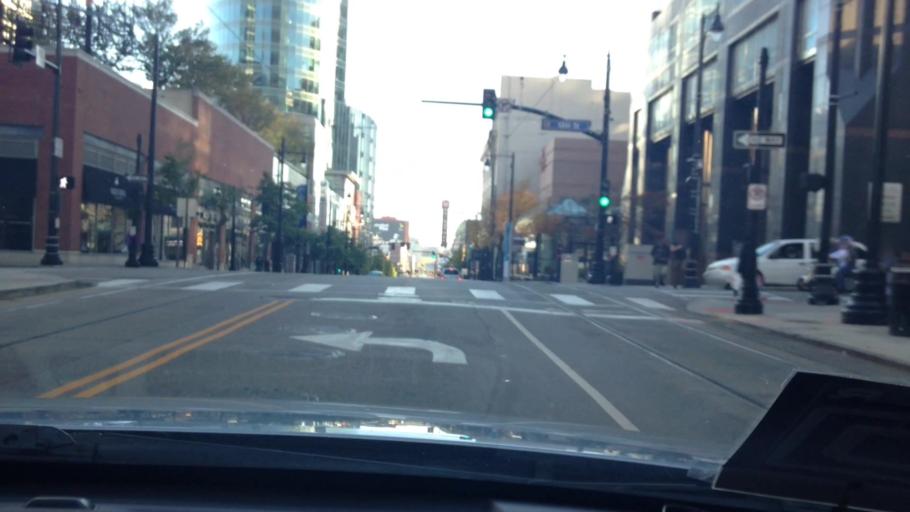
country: US
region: Missouri
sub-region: Jackson County
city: Kansas City
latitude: 39.1005
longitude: -94.5832
